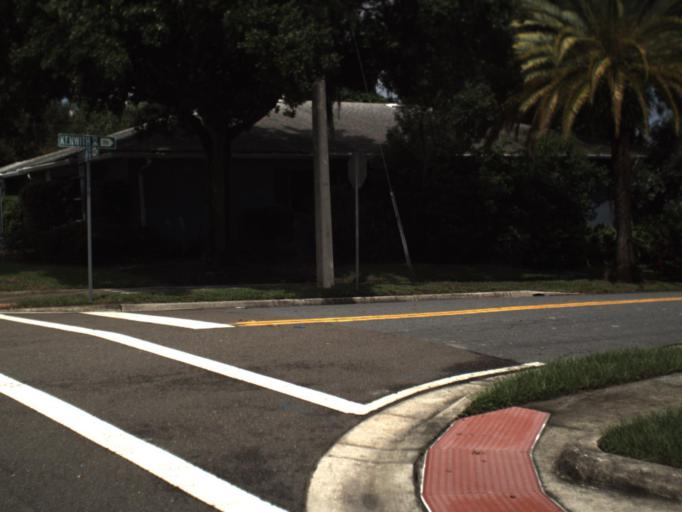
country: US
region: Florida
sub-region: Polk County
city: Lakeland
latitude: 28.0217
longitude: -81.9570
